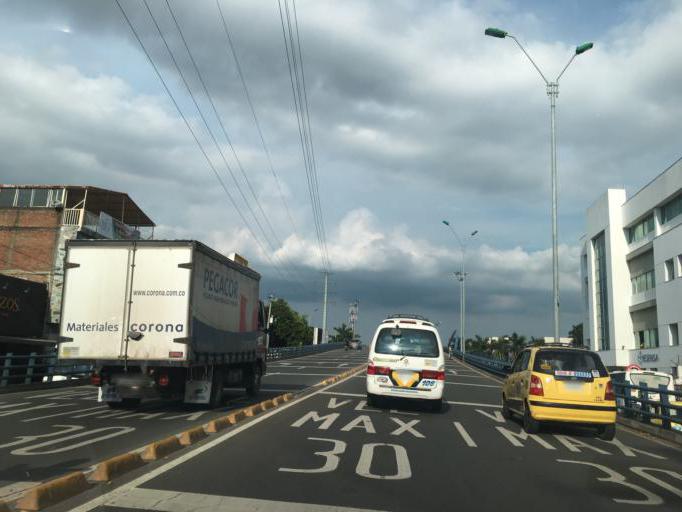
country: CO
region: Valle del Cauca
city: Cali
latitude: 3.4162
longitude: -76.5384
